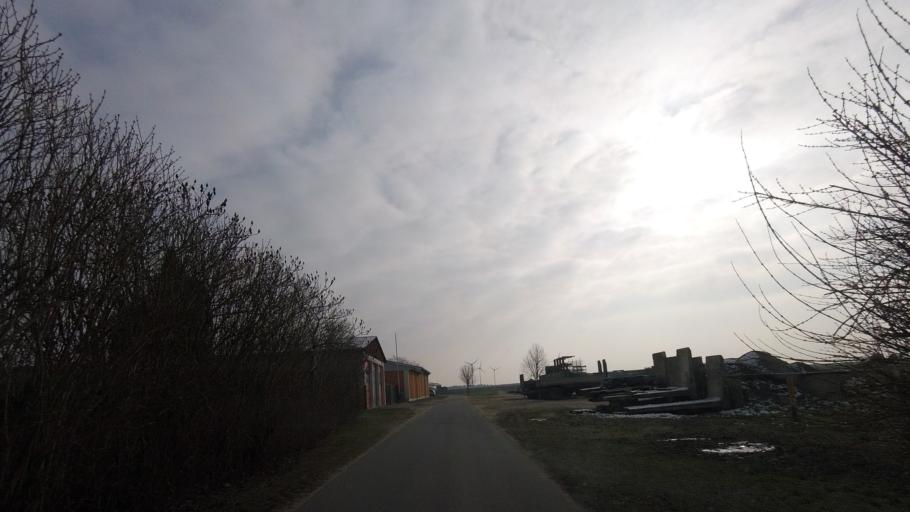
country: DE
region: Brandenburg
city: Juterbog
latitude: 51.9164
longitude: 13.0899
